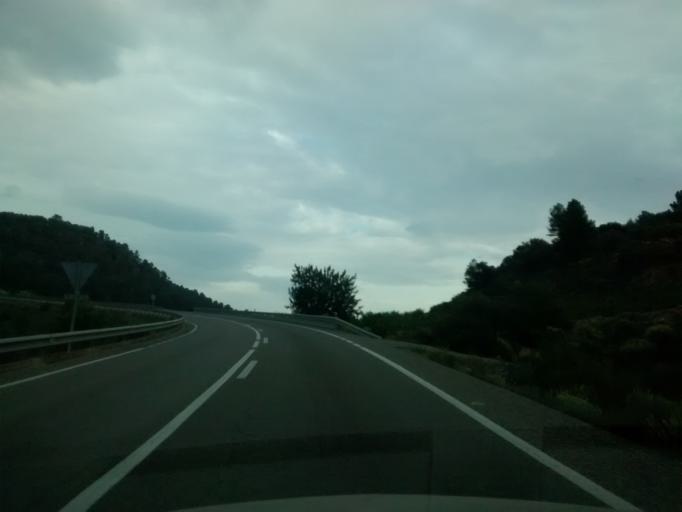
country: ES
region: Catalonia
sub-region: Provincia de Tarragona
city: Benifallet
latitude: 40.9917
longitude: 0.5159
